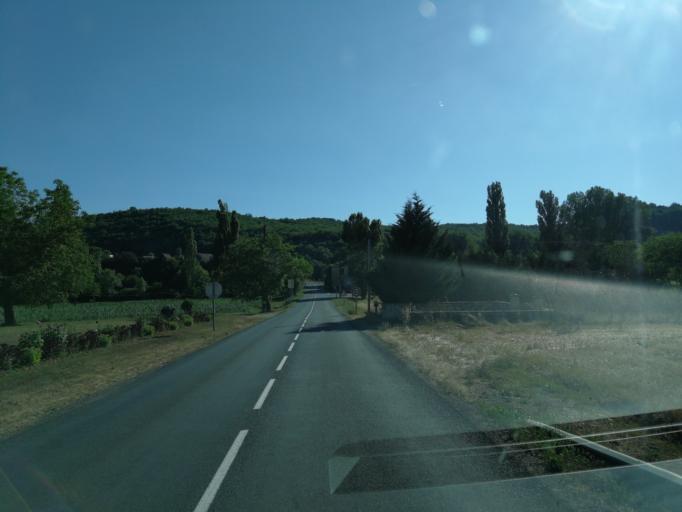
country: FR
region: Midi-Pyrenees
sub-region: Departement du Lot
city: Salviac
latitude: 44.7080
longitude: 1.2971
